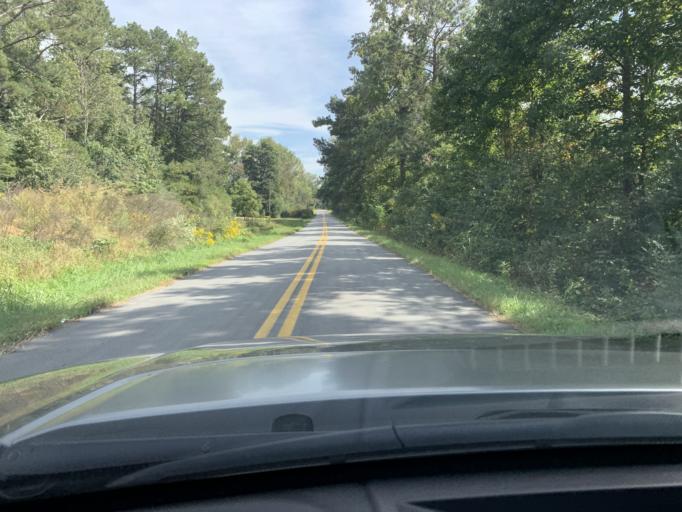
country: US
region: Georgia
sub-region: Polk County
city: Cedartown
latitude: 33.9472
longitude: -85.3726
